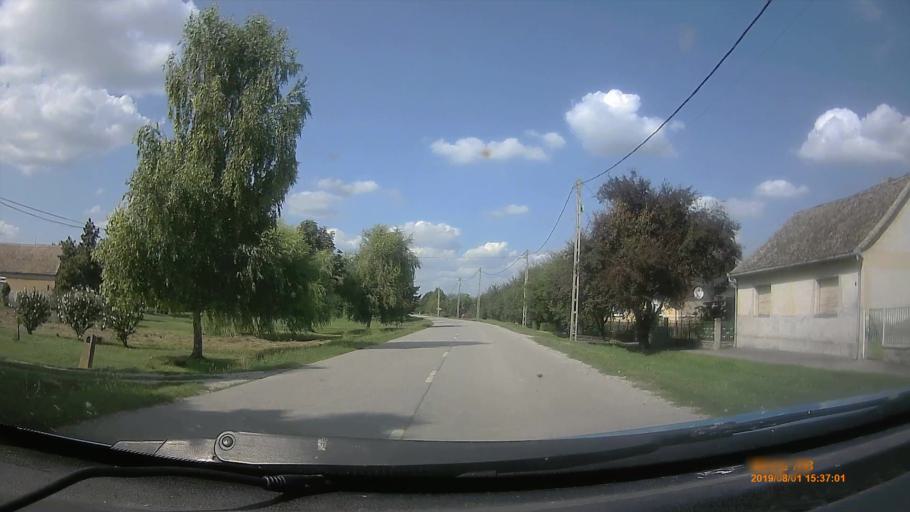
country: HU
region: Baranya
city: Szentlorinc
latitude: 45.9709
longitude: 17.9187
